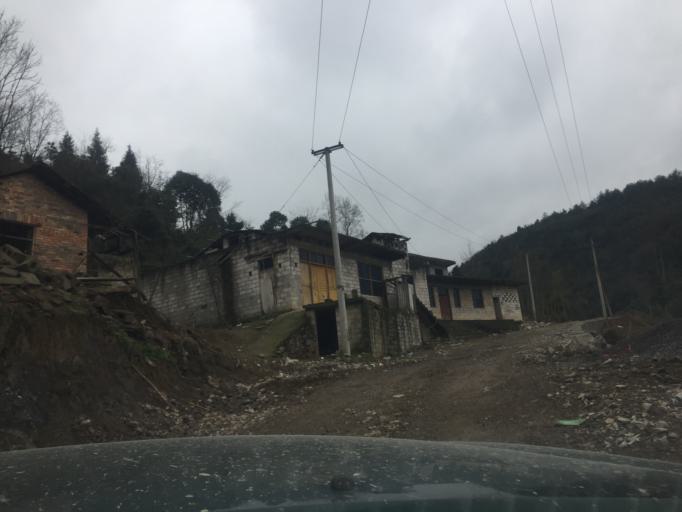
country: CN
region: Guizhou Sheng
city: Jiancha
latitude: 28.1936
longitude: 107.9843
